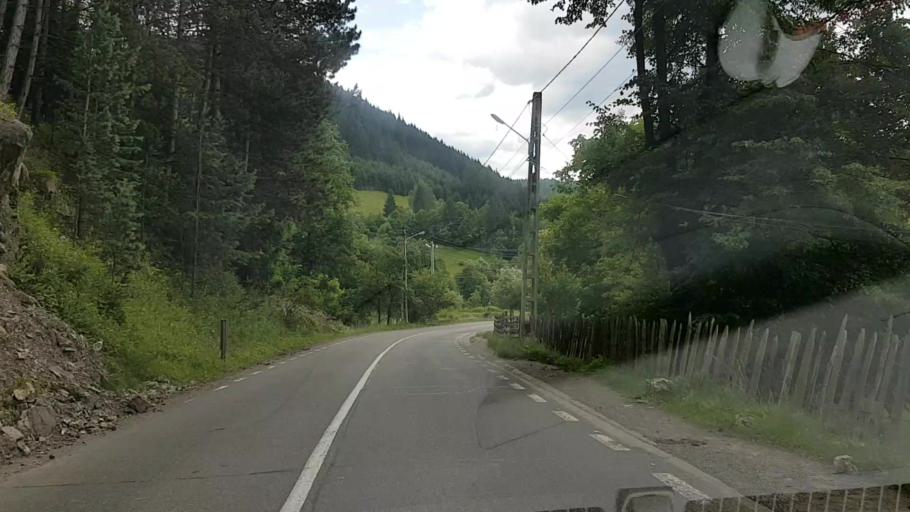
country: RO
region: Suceava
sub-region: Comuna Brosteni
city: Brosteni
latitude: 47.2299
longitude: 25.7444
